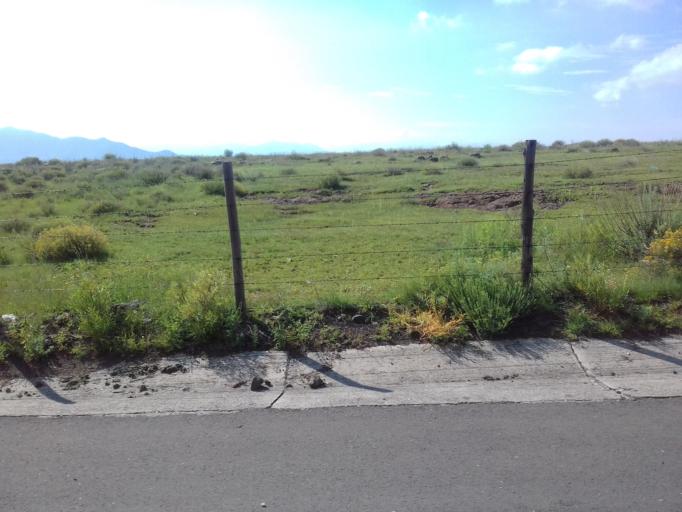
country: LS
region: Thaba-Tseka
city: Thaba-Tseka
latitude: -29.5186
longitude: 28.6185
